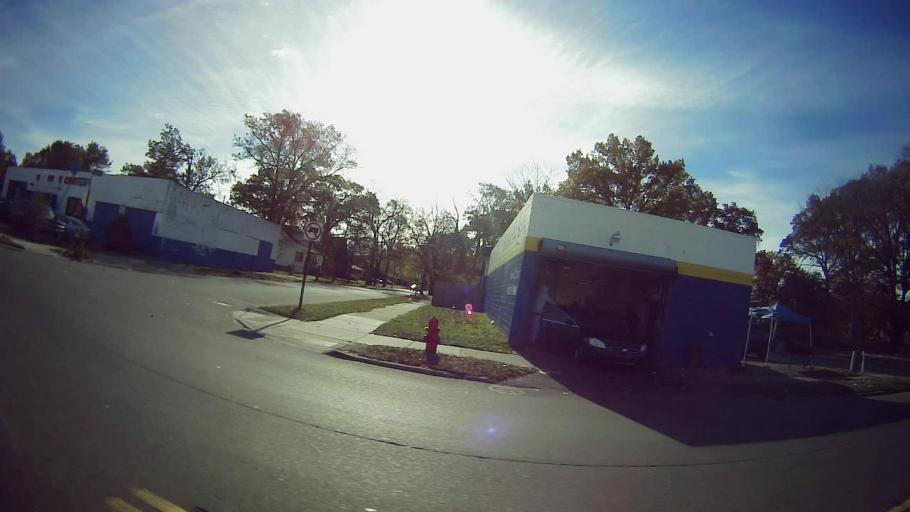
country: US
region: Michigan
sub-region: Wayne County
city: Hamtramck
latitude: 42.4332
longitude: -83.0627
